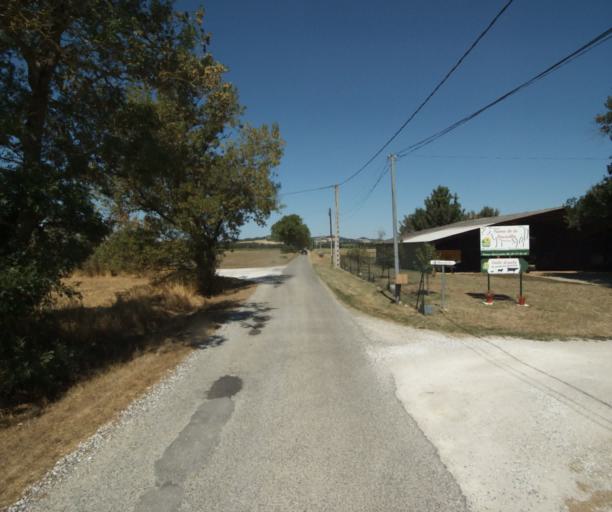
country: FR
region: Midi-Pyrenees
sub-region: Departement de la Haute-Garonne
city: Revel
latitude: 43.4831
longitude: 1.9693
